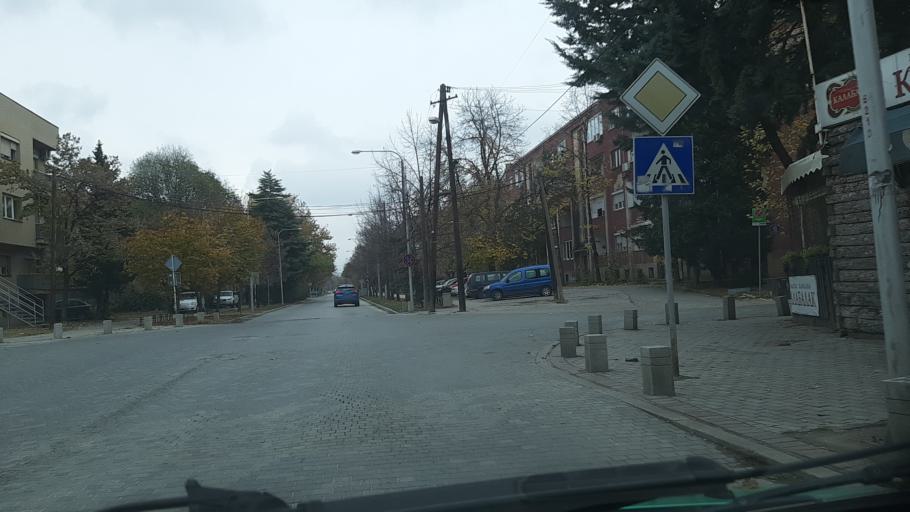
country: MK
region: Karpos
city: Skopje
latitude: 41.9901
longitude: 21.4402
